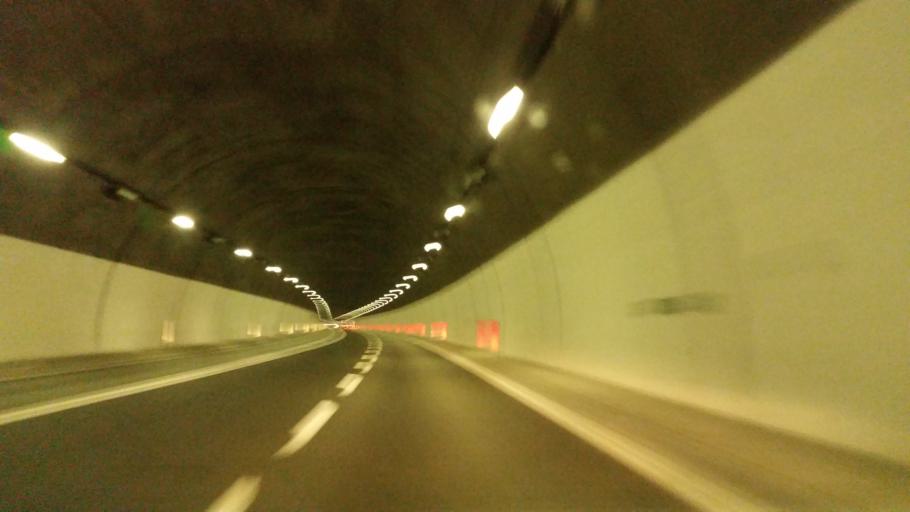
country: IT
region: Aosta Valley
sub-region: Valle d'Aosta
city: Villair-Amerique
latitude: 45.7446
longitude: 7.3815
